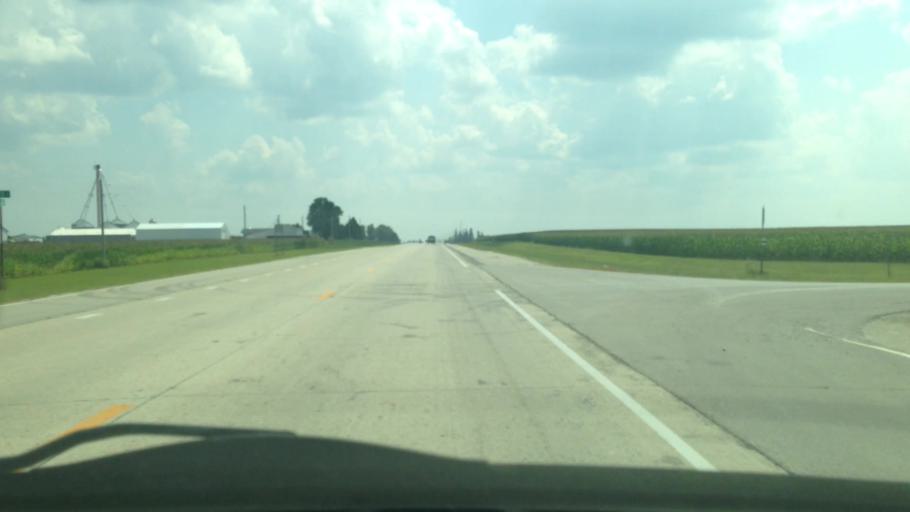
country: US
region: Minnesota
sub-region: Fillmore County
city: Spring Valley
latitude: 43.6604
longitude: -92.3896
